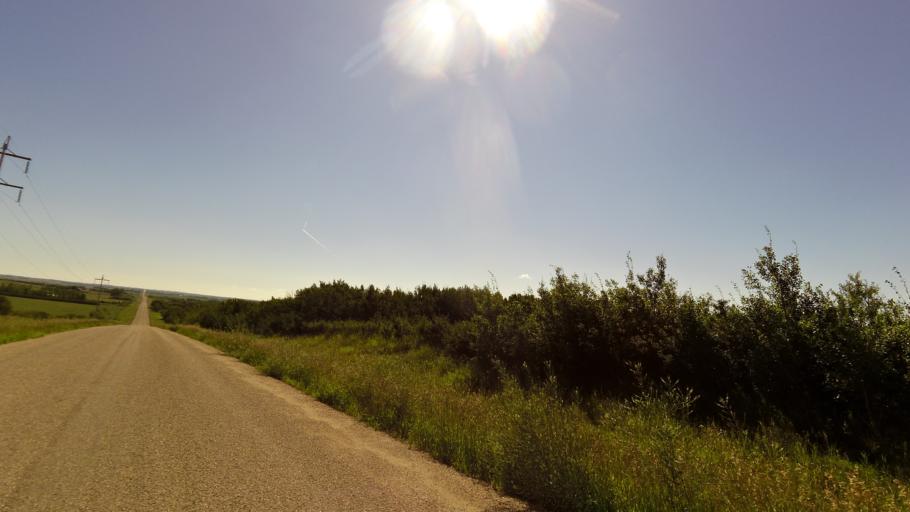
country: CA
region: Alberta
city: Wainwright
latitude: 52.8725
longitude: -111.0394
